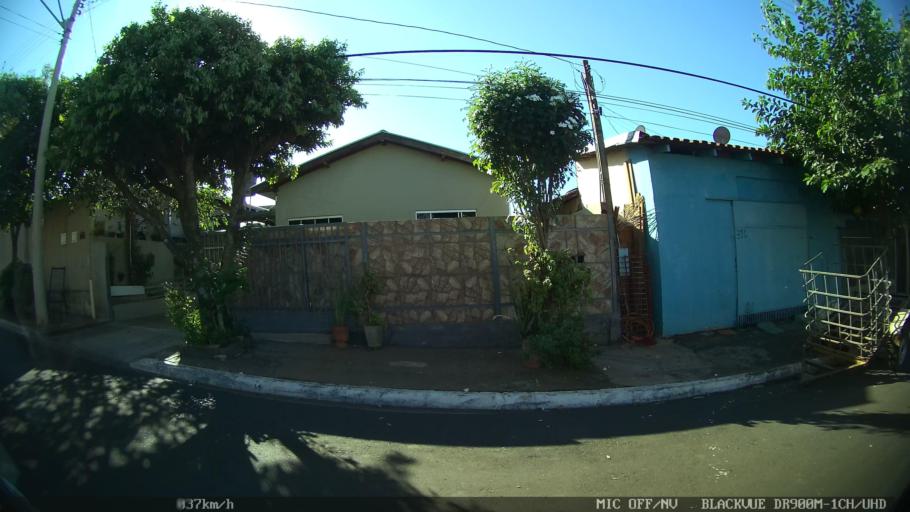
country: BR
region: Sao Paulo
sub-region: Olimpia
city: Olimpia
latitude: -20.7245
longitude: -48.8921
